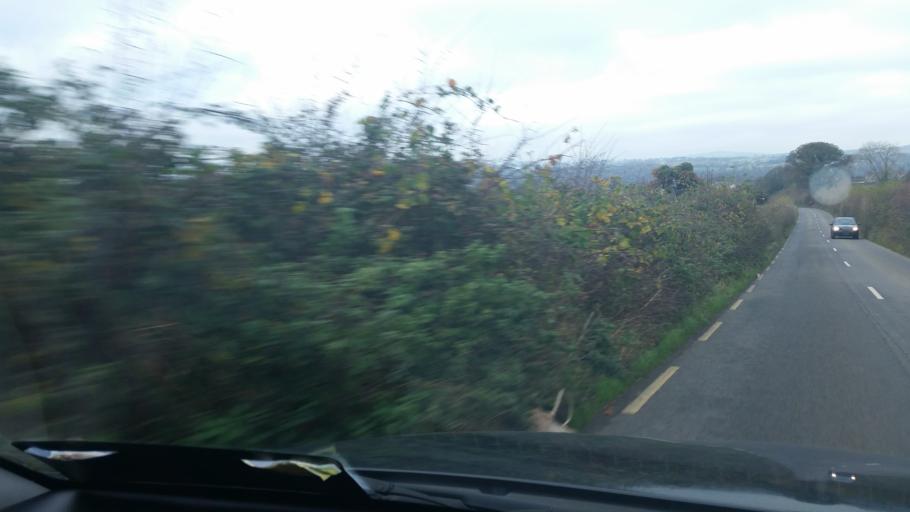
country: IE
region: Leinster
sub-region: Lu
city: Tullyallen
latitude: 53.7062
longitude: -6.4085
